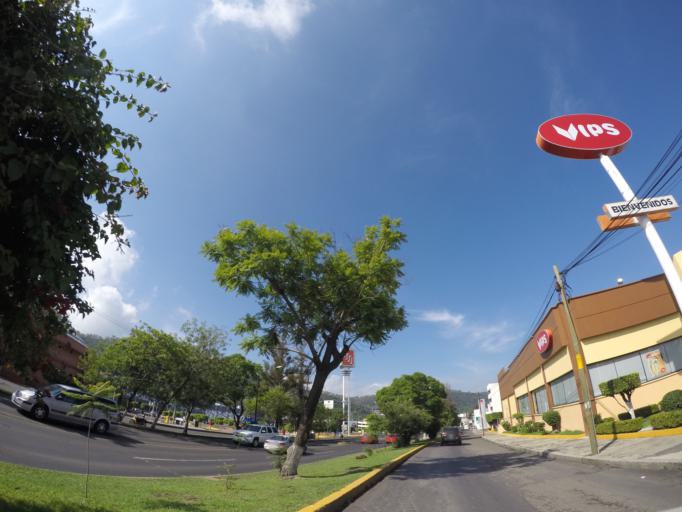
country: MX
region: Michoacan
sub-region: Morelia
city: Puerto de Buenavista (Lazaro Cardenas)
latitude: 19.6898
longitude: -101.1511
